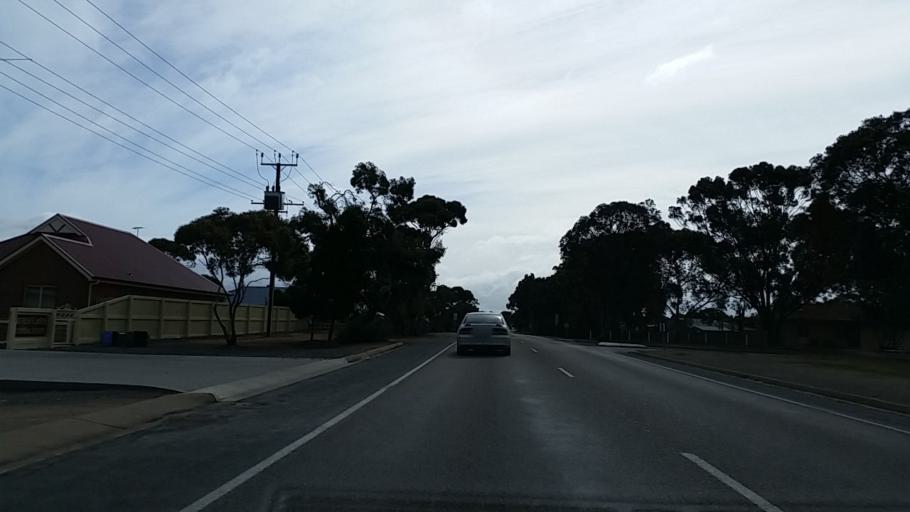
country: AU
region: South Australia
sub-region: Murray Bridge
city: Murray Bridge
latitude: -35.1461
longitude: 139.2860
